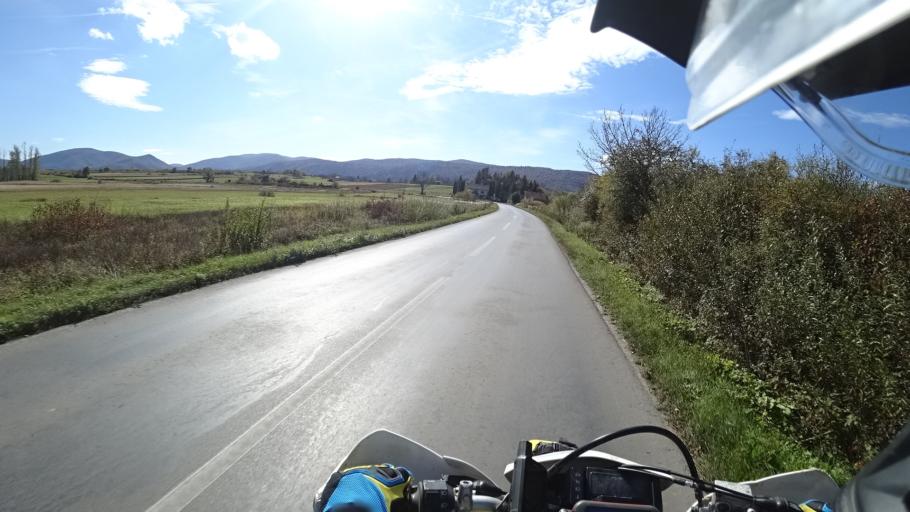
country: HR
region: Karlovacka
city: Plaski
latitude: 45.0970
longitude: 15.3531
